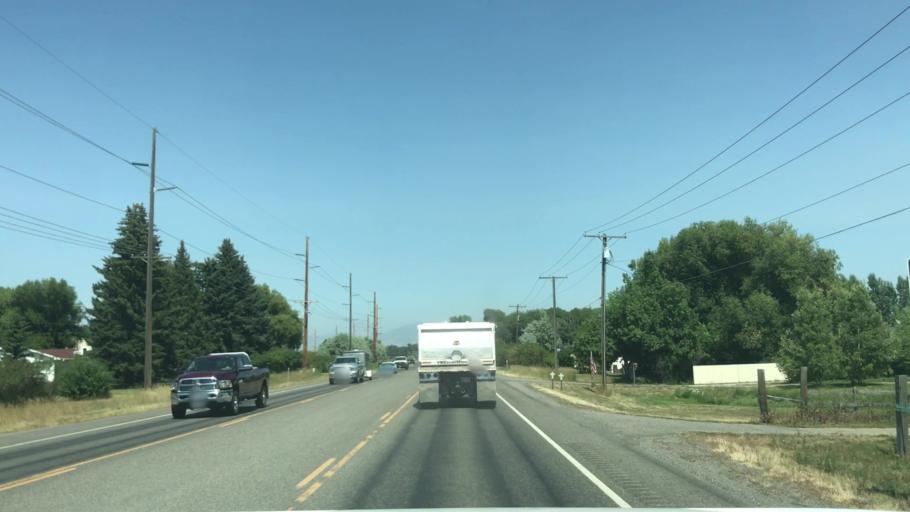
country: US
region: Montana
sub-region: Gallatin County
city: Four Corners
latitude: 45.6556
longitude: -111.1877
